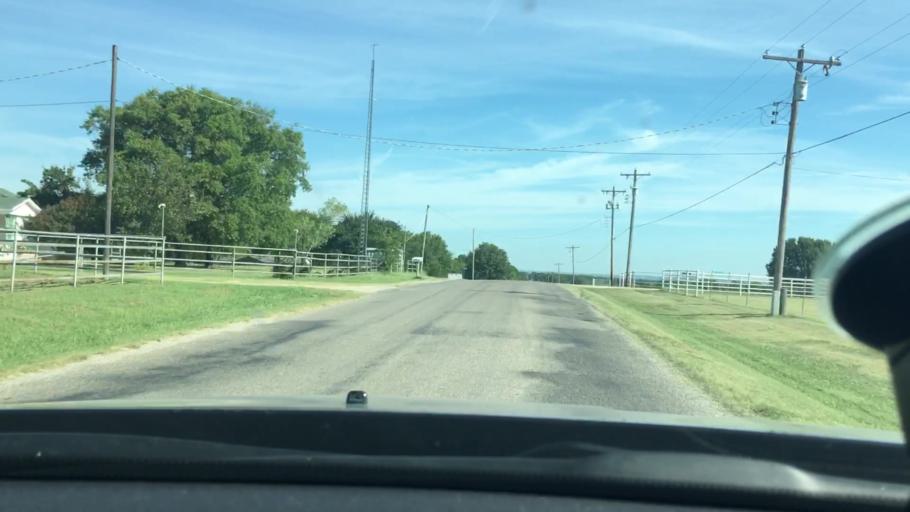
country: US
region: Oklahoma
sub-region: Carter County
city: Lone Grove
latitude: 34.2243
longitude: -97.2474
